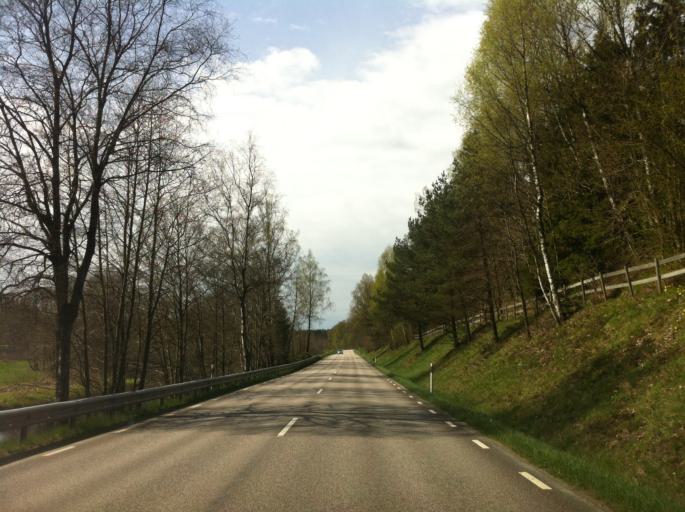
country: SE
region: Vaestra Goetaland
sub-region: Marks Kommun
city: Horred
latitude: 57.1589
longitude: 12.7396
